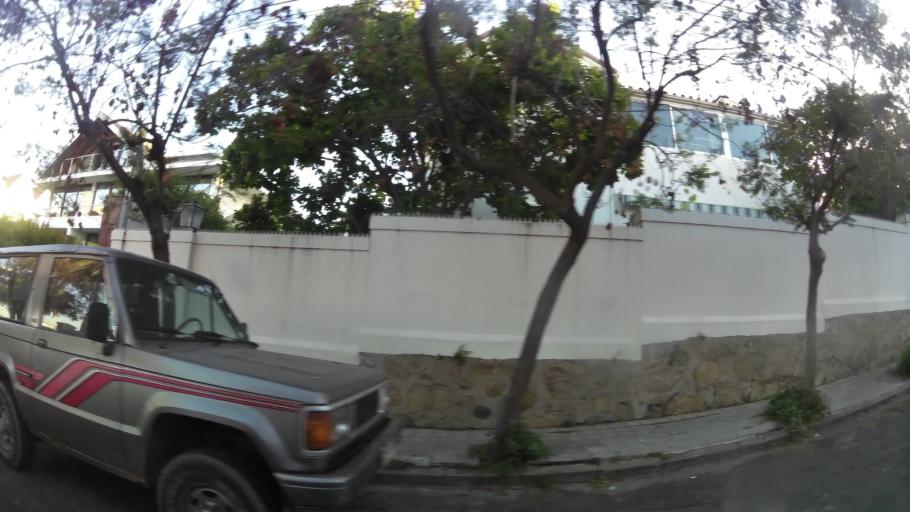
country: CL
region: Valparaiso
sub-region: Provincia de Valparaiso
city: Vina del Mar
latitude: -33.0218
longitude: -71.5628
